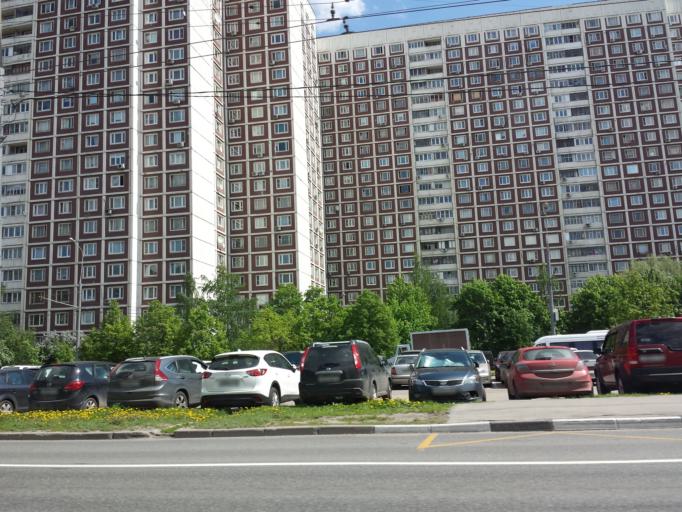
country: RU
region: Moscow
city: Lianozovo
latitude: 55.9026
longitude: 37.5872
